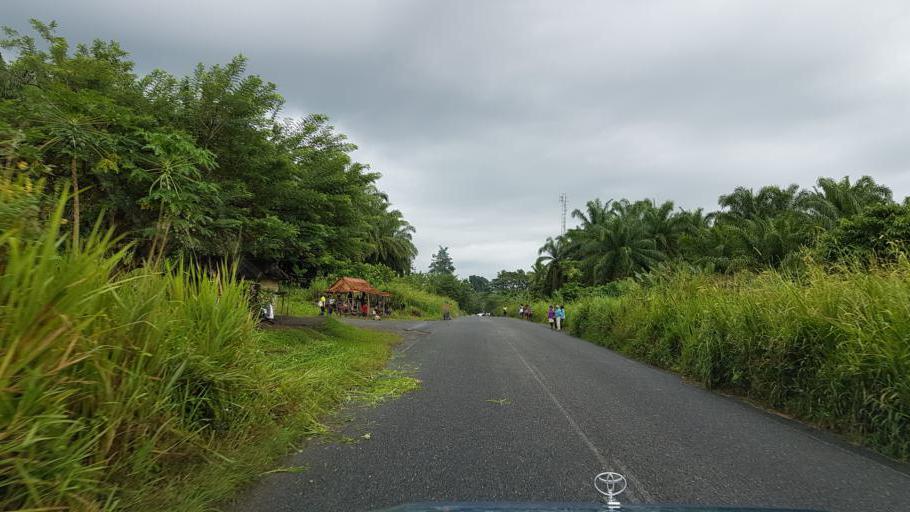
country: PG
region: Northern Province
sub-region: Sohe
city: Popondetta
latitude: -8.8269
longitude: 148.2636
